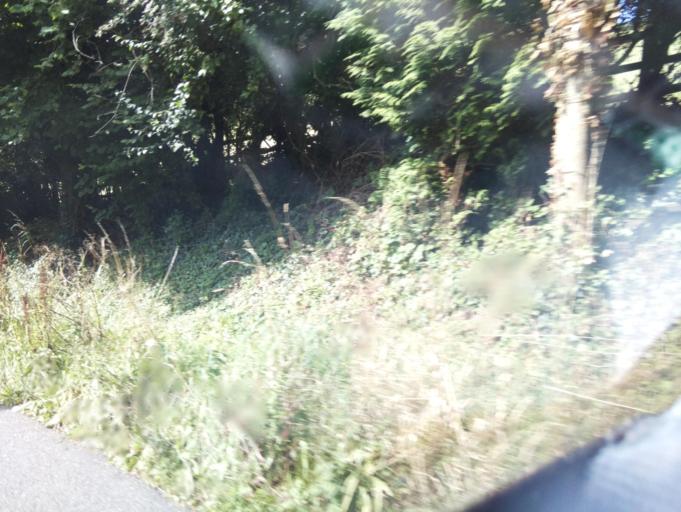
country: GB
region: England
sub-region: Devon
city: Dartmouth
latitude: 50.3573
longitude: -3.5629
